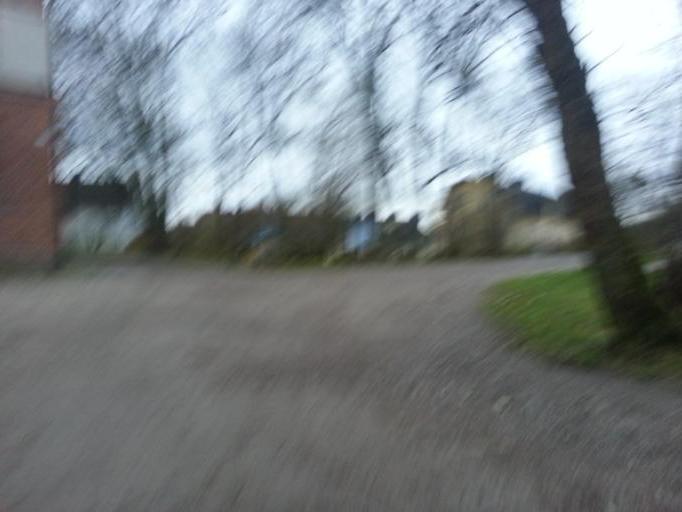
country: FI
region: Uusimaa
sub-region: Helsinki
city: Helsinki
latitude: 60.1424
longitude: 24.9862
